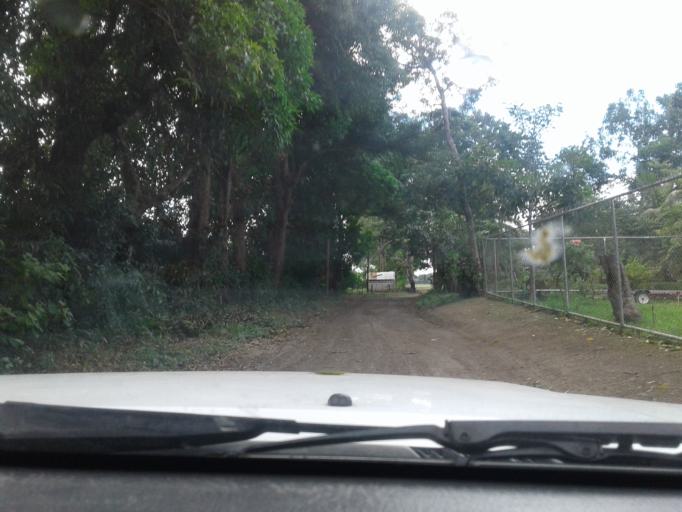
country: NI
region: Rivas
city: Potosi
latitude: 11.4811
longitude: -85.8396
